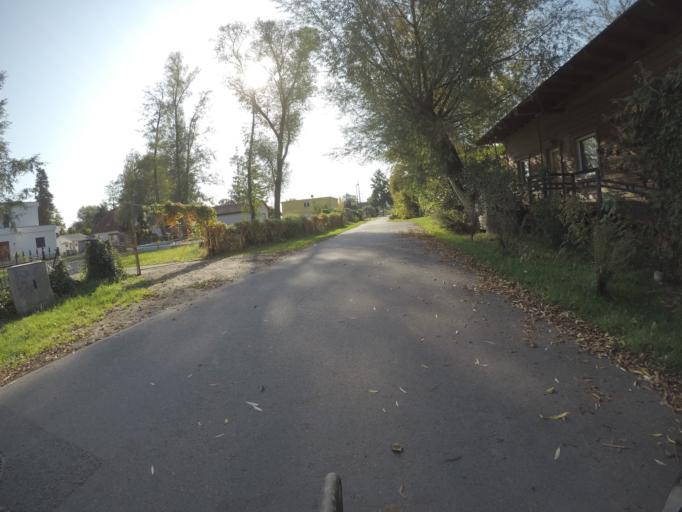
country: DE
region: Brandenburg
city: Oranienburg
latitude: 52.7369
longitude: 13.2544
